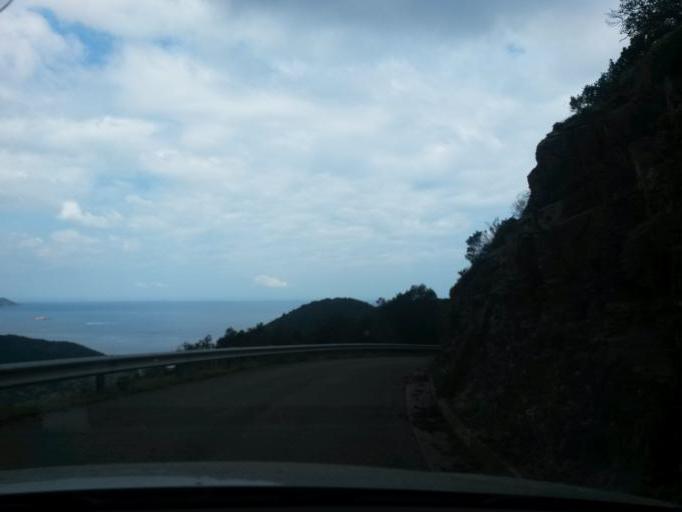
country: IT
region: Tuscany
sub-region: Provincia di Livorno
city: Rio nell'Elba
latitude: 42.8248
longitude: 10.3923
